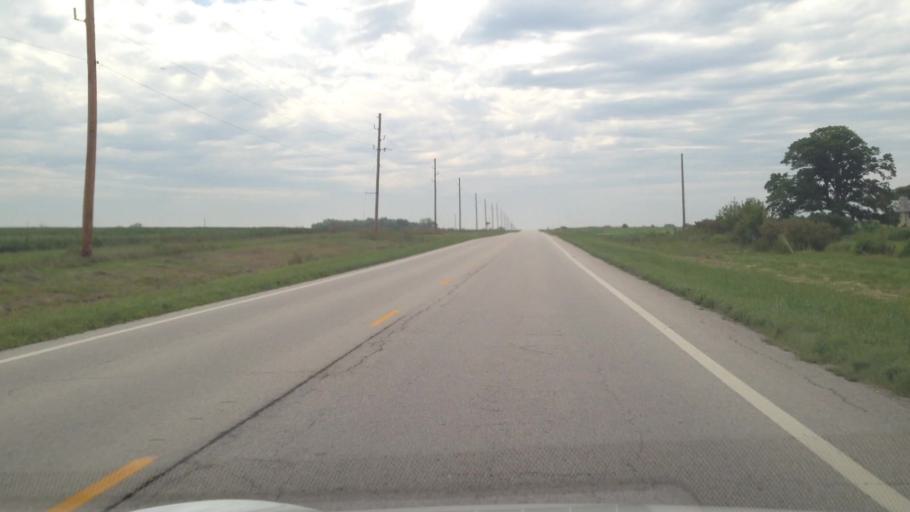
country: US
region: Kansas
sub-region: Allen County
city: Iola
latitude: 37.9412
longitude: -95.1701
